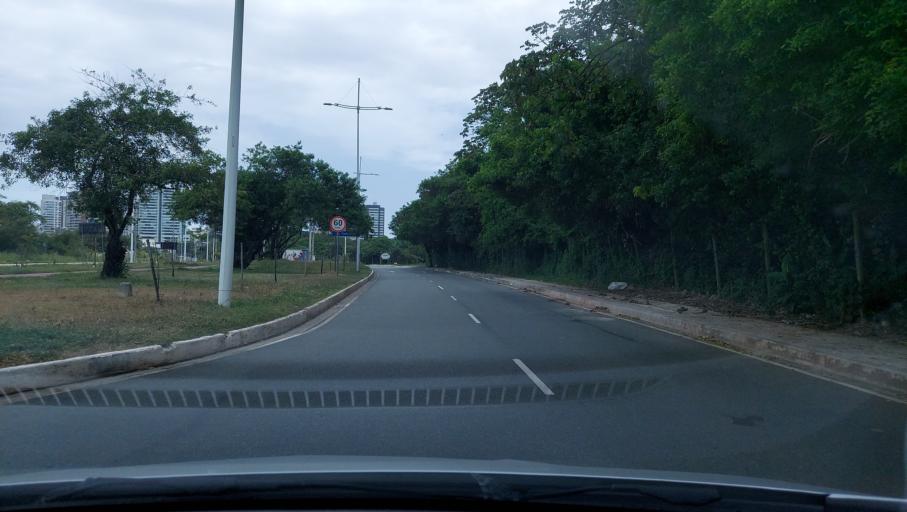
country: BR
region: Bahia
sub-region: Lauro De Freitas
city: Lauro de Freitas
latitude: -12.9549
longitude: -38.3976
